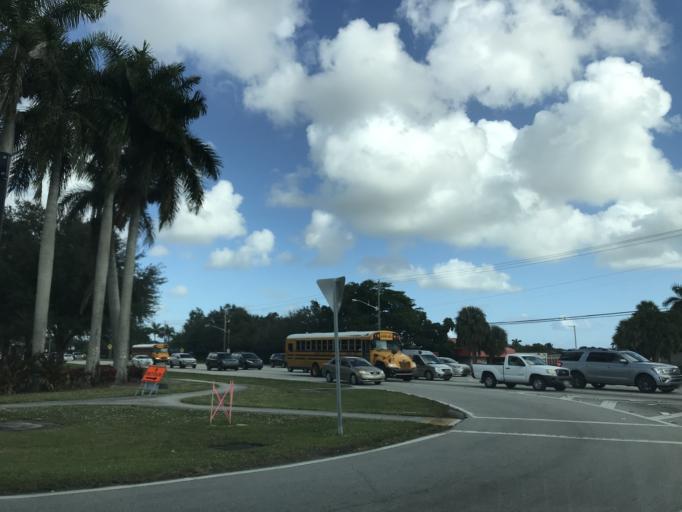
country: US
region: Florida
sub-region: Broward County
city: Margate
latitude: 26.2556
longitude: -80.1956
